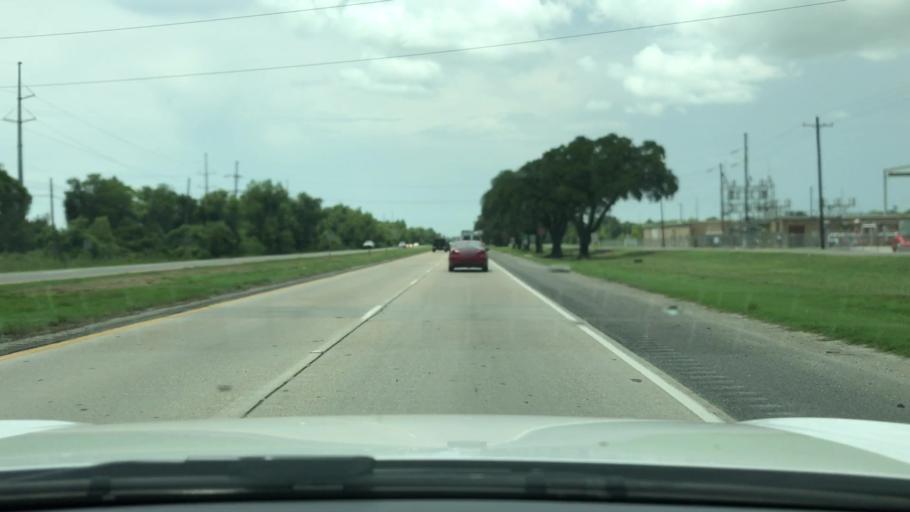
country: US
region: Louisiana
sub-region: West Baton Rouge Parish
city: Addis
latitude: 30.3228
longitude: -91.2526
